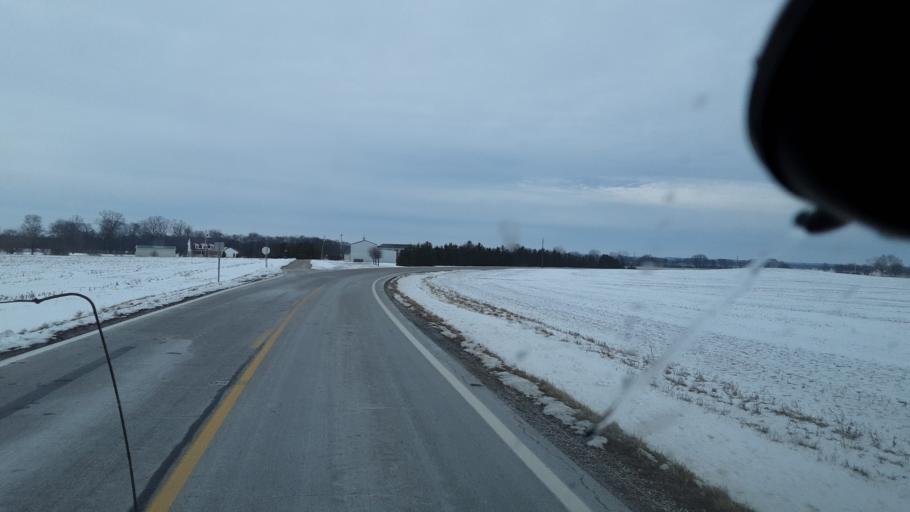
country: US
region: Ohio
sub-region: Pickaway County
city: Circleville
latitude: 39.6253
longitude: -83.0315
